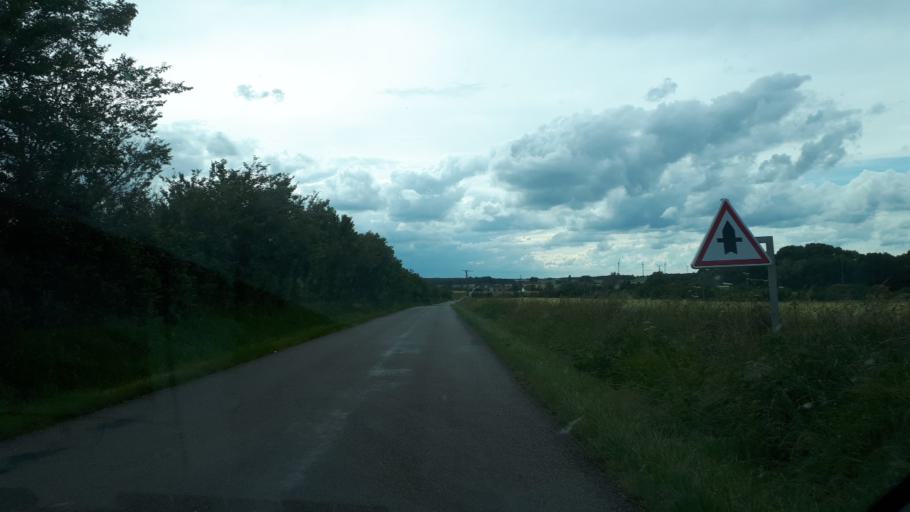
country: FR
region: Centre
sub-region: Departement de l'Indre
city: Reuilly
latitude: 47.0929
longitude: 2.0141
